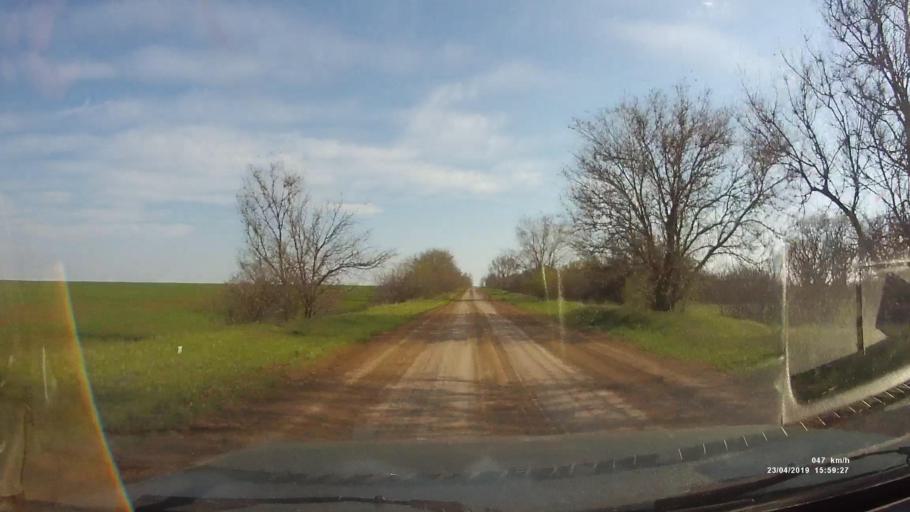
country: RU
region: Rostov
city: Remontnoye
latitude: 46.5167
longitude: 43.1096
